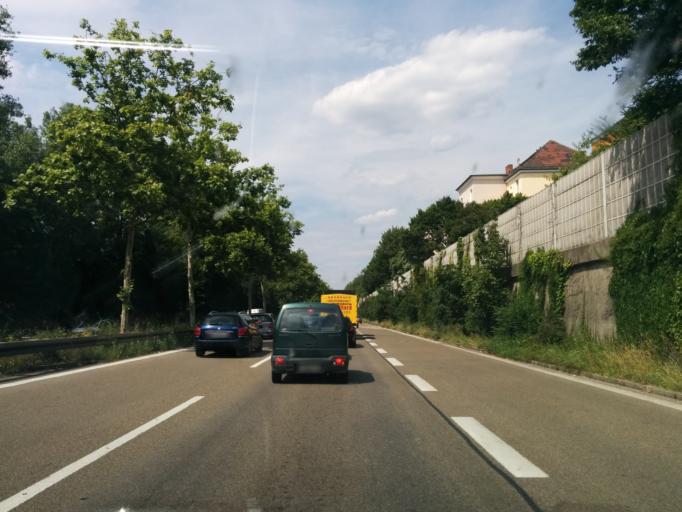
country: DE
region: Bavaria
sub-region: Regierungsbezirk Mittelfranken
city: Nuernberg
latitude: 49.4332
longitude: 11.0632
